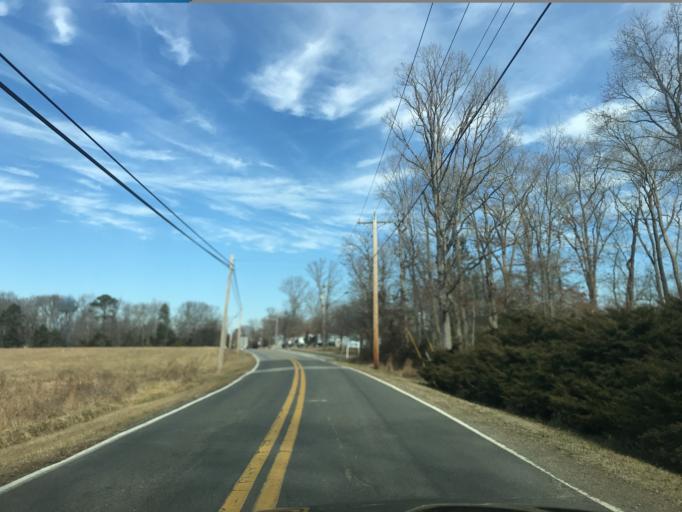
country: US
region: Maryland
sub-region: Charles County
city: La Plata
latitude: 38.5157
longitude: -76.9778
